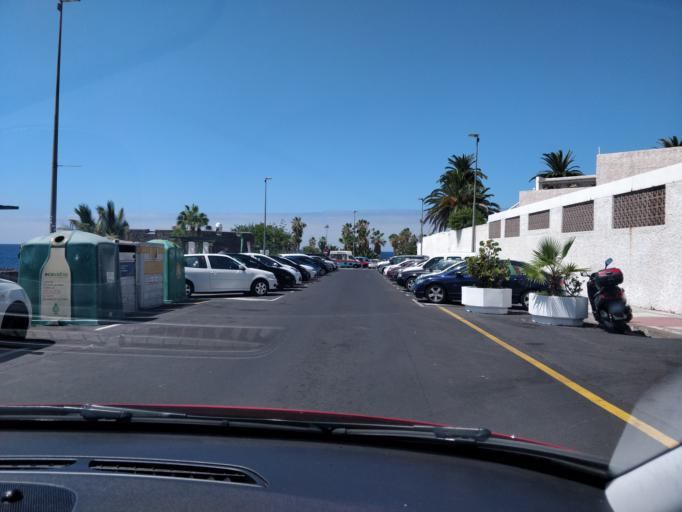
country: ES
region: Canary Islands
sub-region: Provincia de Santa Cruz de Tenerife
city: Puerto de la Cruz
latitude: 28.4133
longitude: -16.5582
